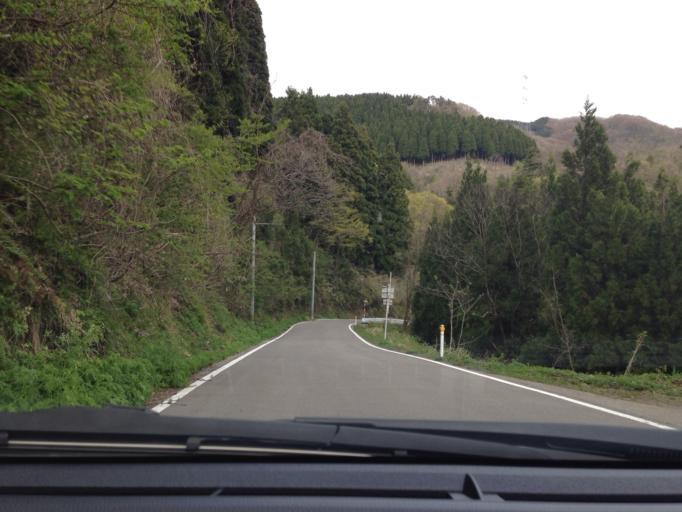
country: JP
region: Toyama
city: Fukumitsu
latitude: 36.5210
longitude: 136.7645
